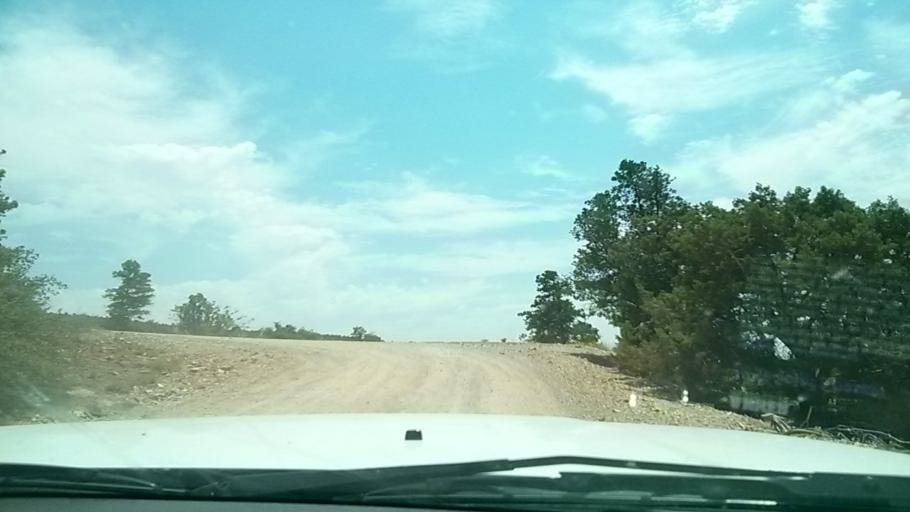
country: US
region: Utah
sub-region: Washington County
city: Toquerville
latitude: 37.2687
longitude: -113.4058
